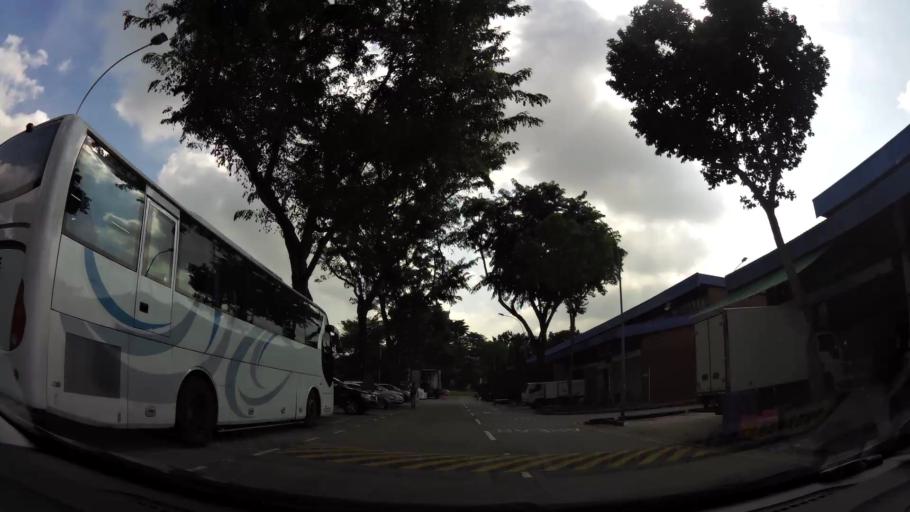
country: SG
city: Singapore
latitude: 1.3218
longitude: 103.8893
